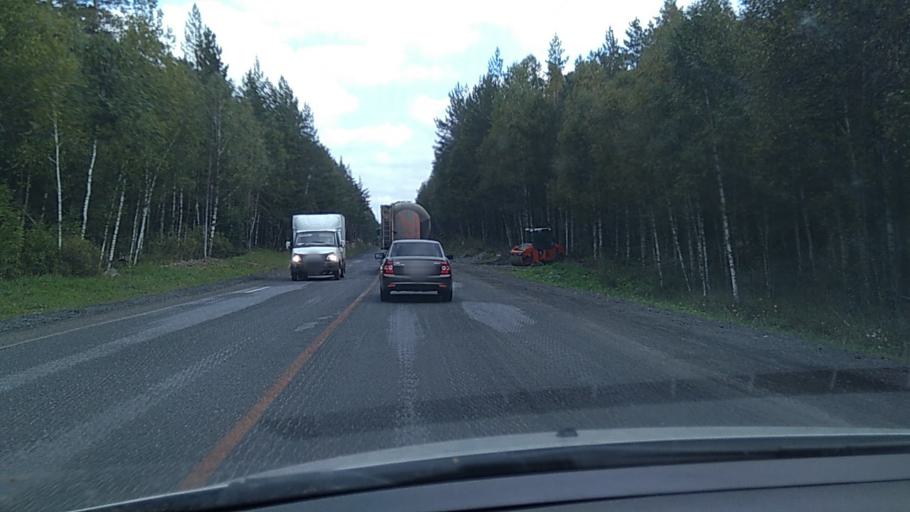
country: RU
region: Chelyabinsk
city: Miass
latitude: 54.9310
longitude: 60.1601
